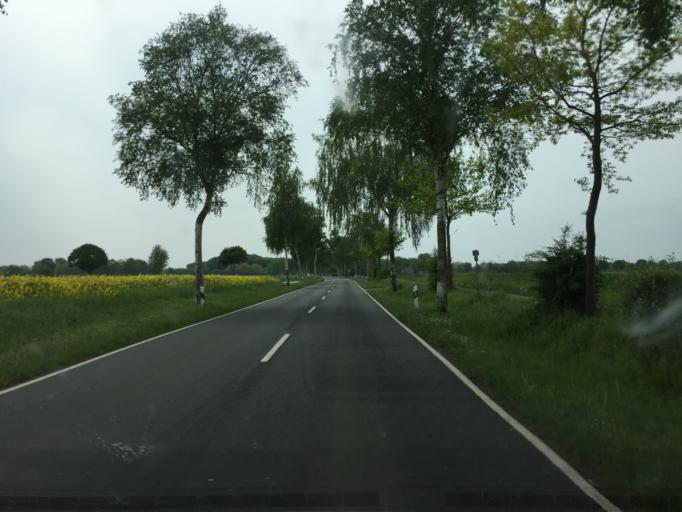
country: DE
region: Lower Saxony
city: Bassum
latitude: 52.8729
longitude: 8.7653
